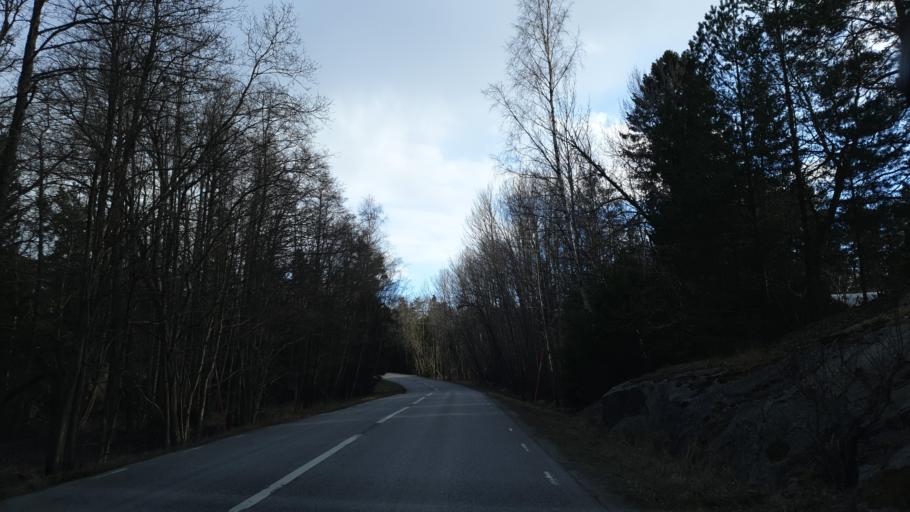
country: SE
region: Stockholm
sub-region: Varmdo Kommun
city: Holo
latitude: 59.3329
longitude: 18.7191
